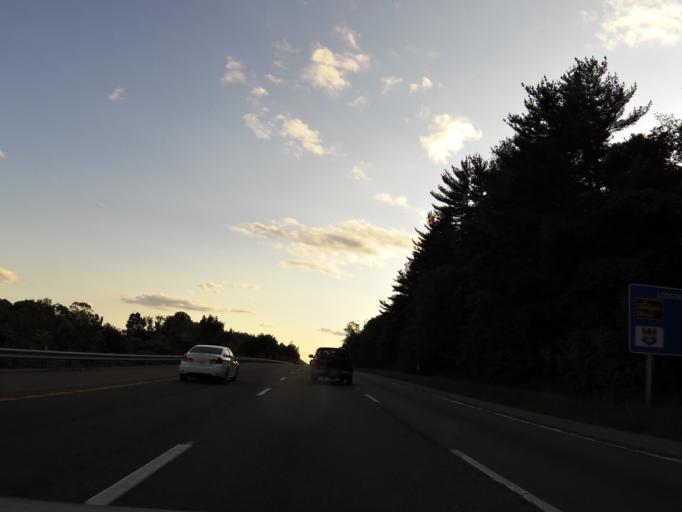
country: US
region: Virginia
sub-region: City of Bristol
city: Bristol
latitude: 36.6145
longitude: -82.2026
